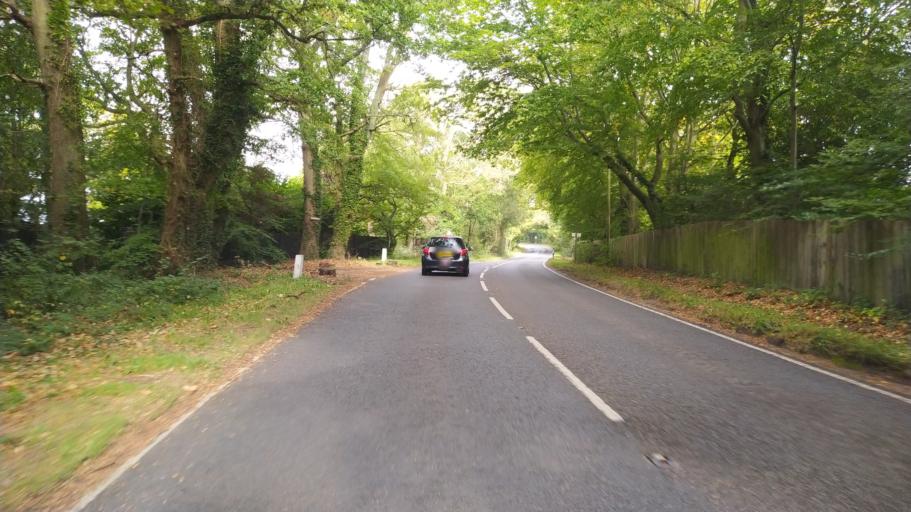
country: GB
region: England
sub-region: Hampshire
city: Lymington
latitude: 50.7755
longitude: -1.5528
